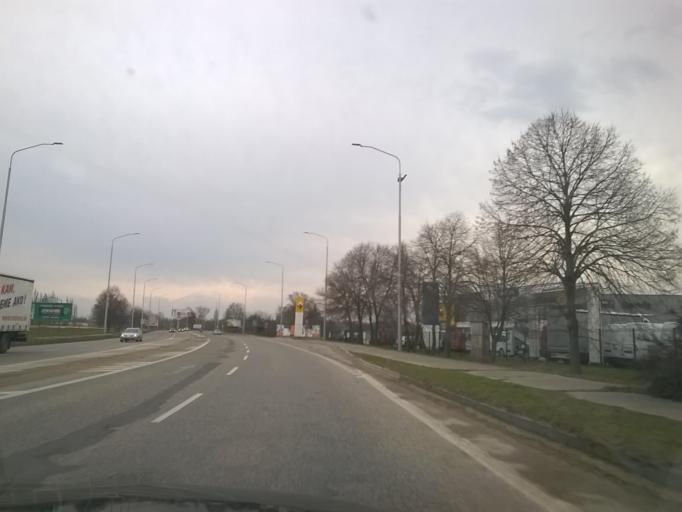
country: SK
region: Nitriansky
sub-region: Okres Nitra
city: Nitra
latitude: 48.3183
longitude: 18.0539
